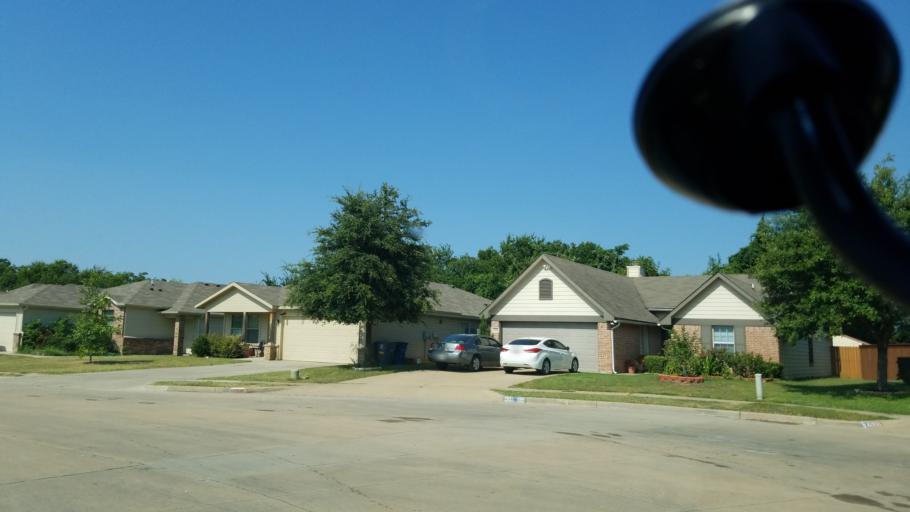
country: US
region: Texas
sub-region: Dallas County
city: Cockrell Hill
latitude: 32.7127
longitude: -96.8720
